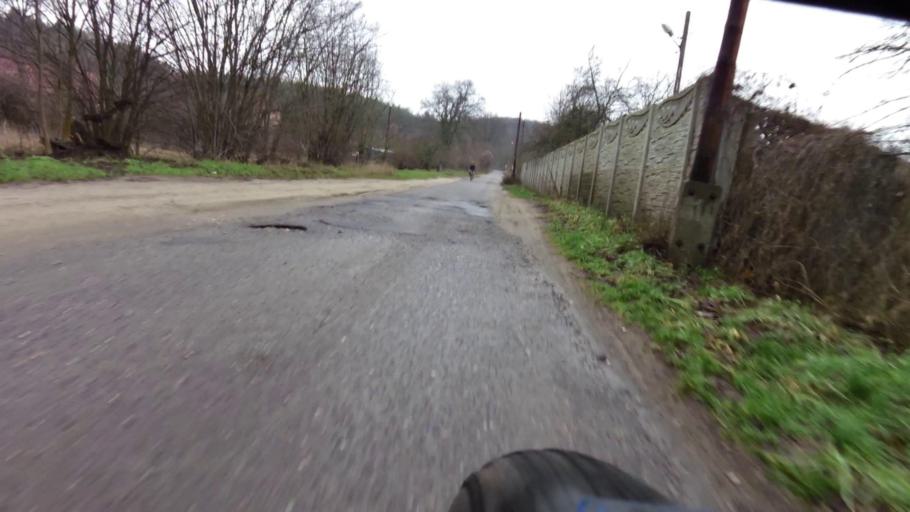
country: PL
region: Lubusz
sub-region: Powiat gorzowski
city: Kostrzyn nad Odra
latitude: 52.6216
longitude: 14.7097
